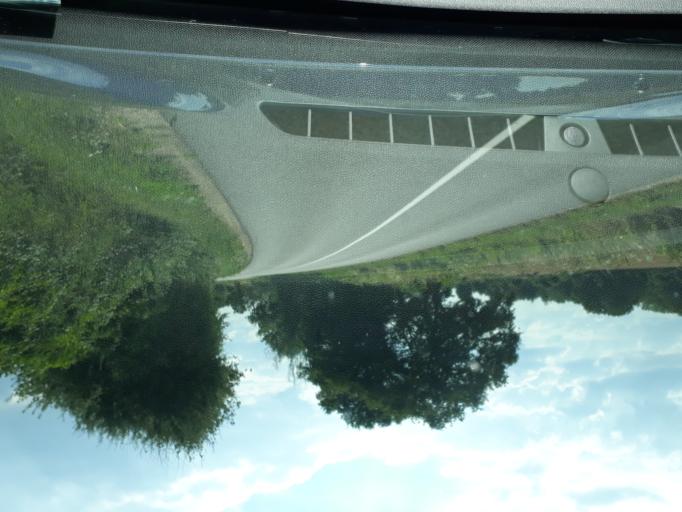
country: FR
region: Centre
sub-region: Departement du Cher
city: Nerondes
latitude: 47.0486
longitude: 2.8818
